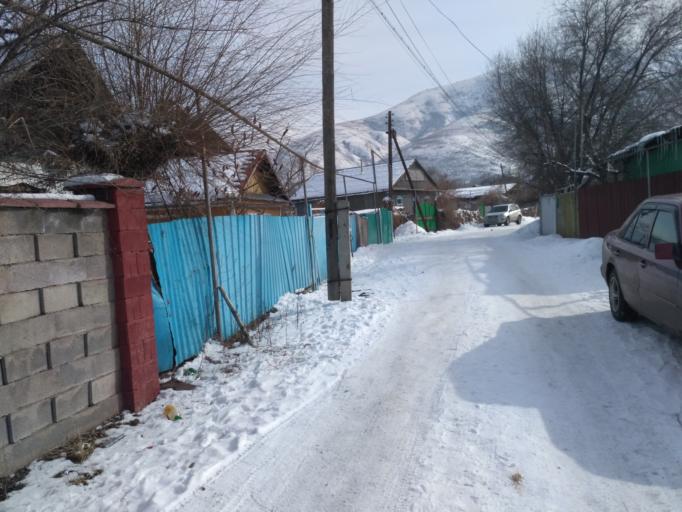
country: KZ
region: Almaty Oblysy
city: Burunday
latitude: 43.1593
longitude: 76.4038
